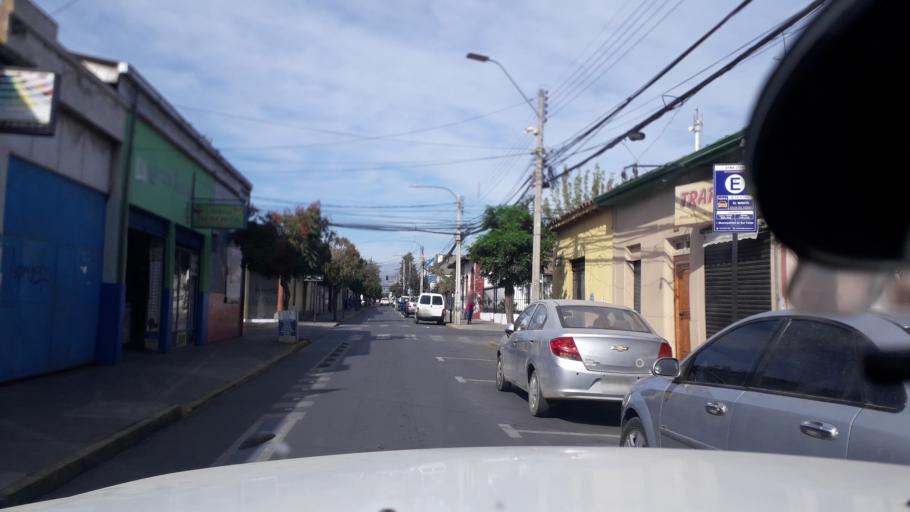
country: CL
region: Valparaiso
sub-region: Provincia de San Felipe
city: San Felipe
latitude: -32.7503
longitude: -70.7289
